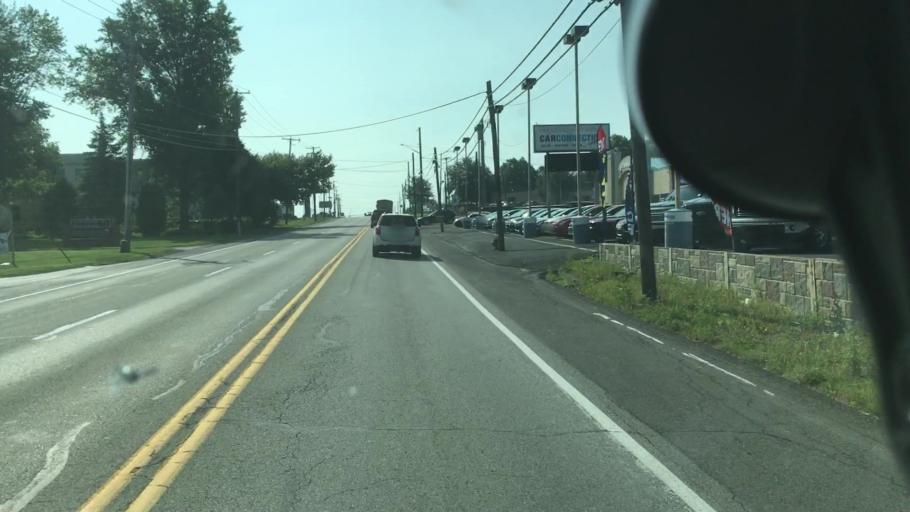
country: US
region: Pennsylvania
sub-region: Lawrence County
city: Oakwood
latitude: 41.0153
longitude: -80.4035
